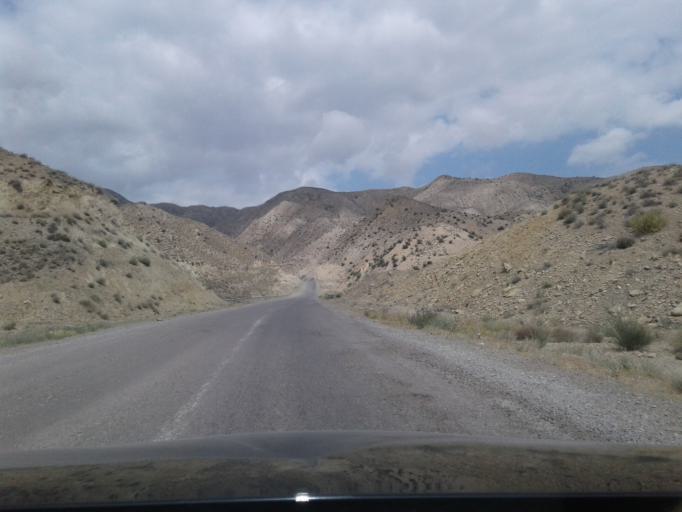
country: TM
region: Ahal
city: Baharly
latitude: 38.5046
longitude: 57.0639
